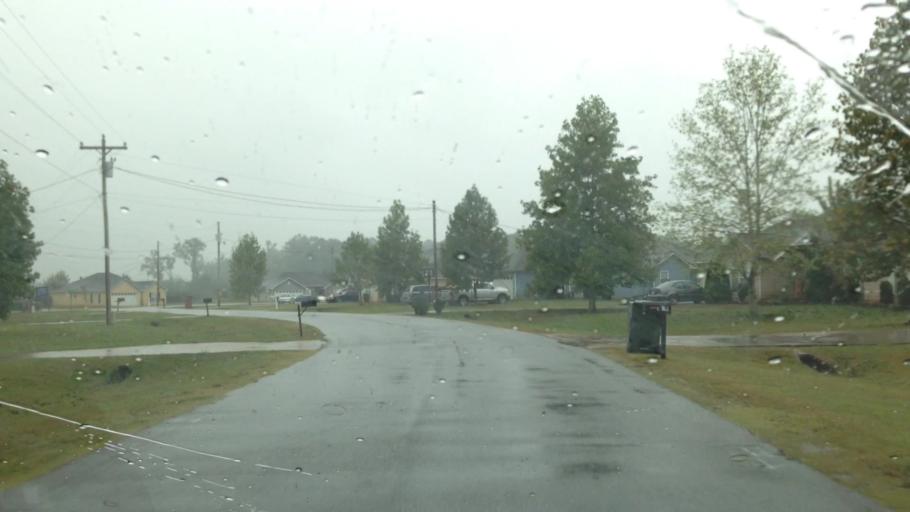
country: US
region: Georgia
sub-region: Muscogee County
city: Columbus
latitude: 32.2643
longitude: -84.9759
